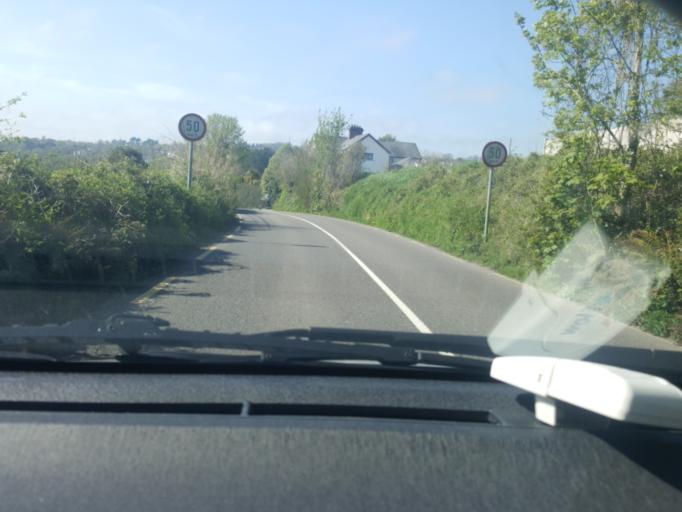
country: IE
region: Munster
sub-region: County Cork
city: Bandon
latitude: 51.7631
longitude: -8.6514
